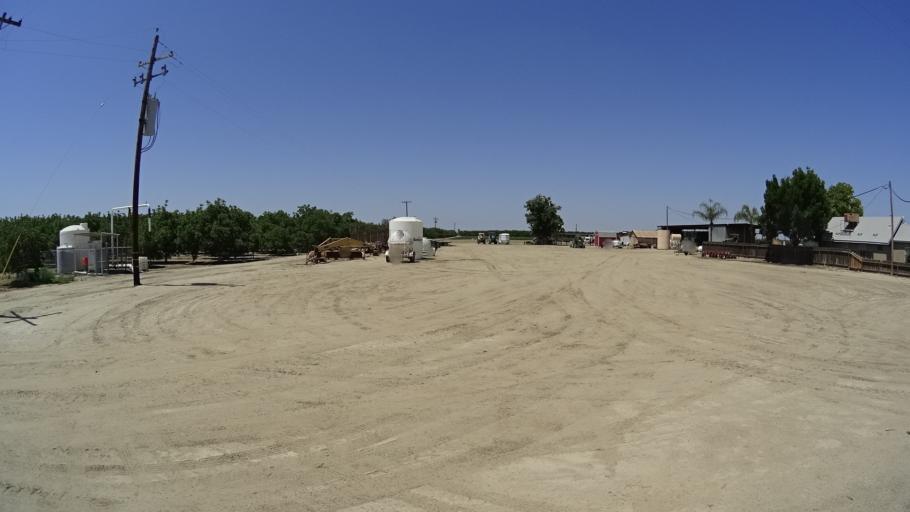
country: US
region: California
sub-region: Kings County
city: Armona
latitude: 36.2913
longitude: -119.7271
